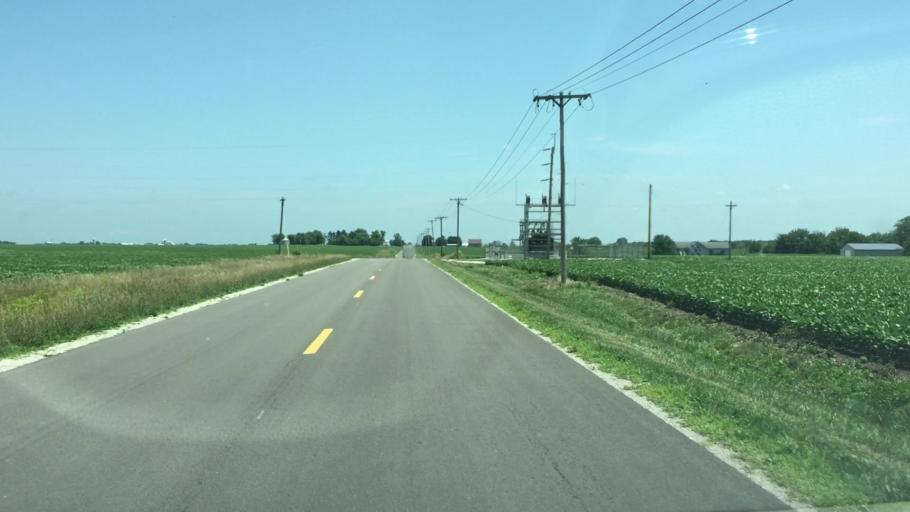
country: US
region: Illinois
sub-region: Hancock County
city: Carthage
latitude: 40.3280
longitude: -91.1822
